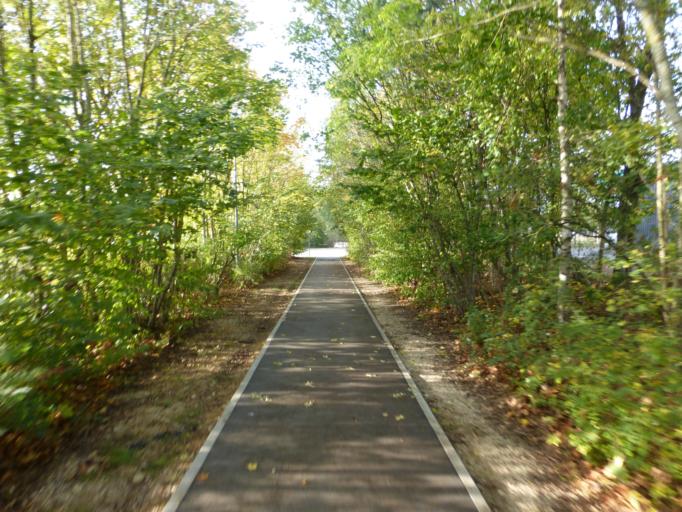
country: FR
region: Lorraine
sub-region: Departement de Meurthe-et-Moselle
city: Laxou
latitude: 48.7038
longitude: 6.1287
